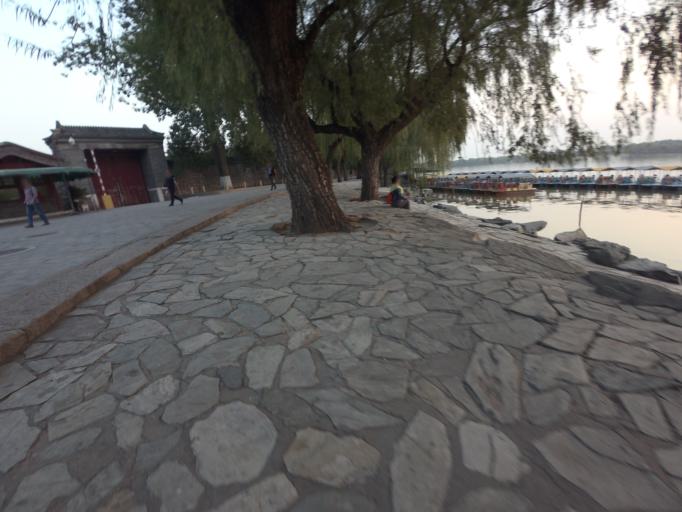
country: CN
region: Beijing
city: Haidian
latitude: 39.9890
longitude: 116.2726
